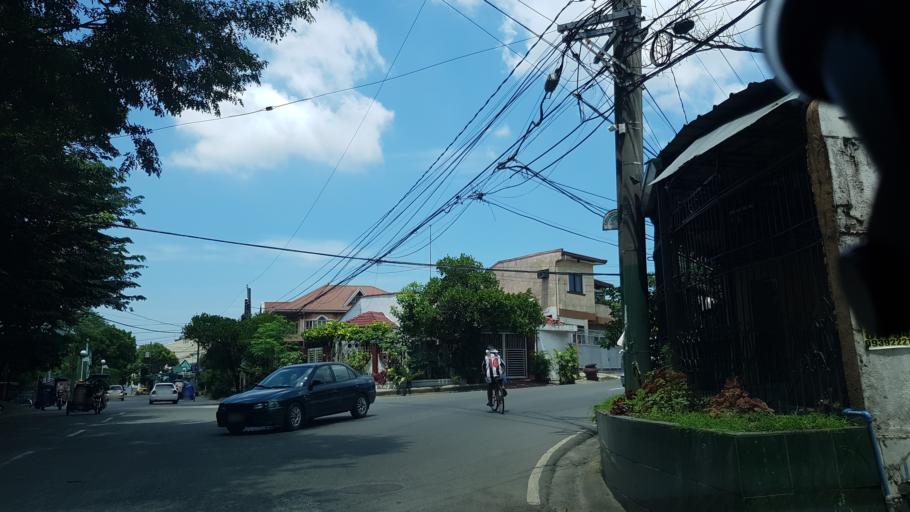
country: PH
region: Calabarzon
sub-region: Province of Rizal
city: Las Pinas
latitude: 14.4337
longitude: 120.9842
